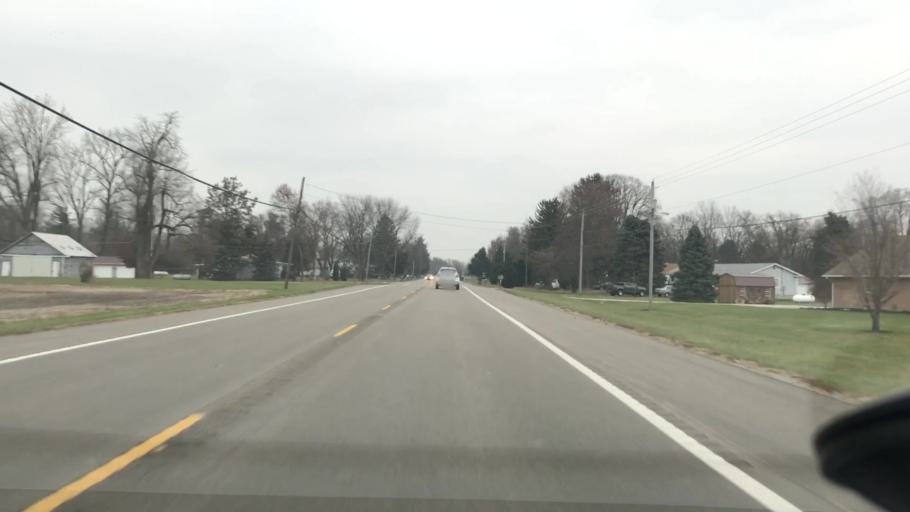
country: US
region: Ohio
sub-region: Greene County
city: Yellow Springs
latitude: 39.8597
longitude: -83.8513
